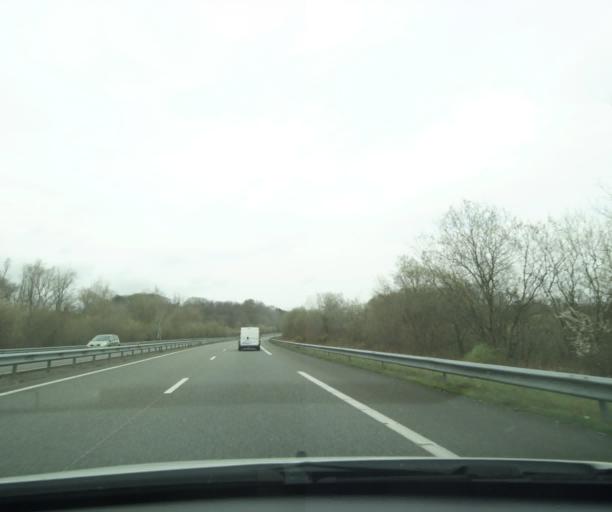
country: FR
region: Aquitaine
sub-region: Departement des Pyrenees-Atlantiques
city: Urt
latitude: 43.4779
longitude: -1.2764
